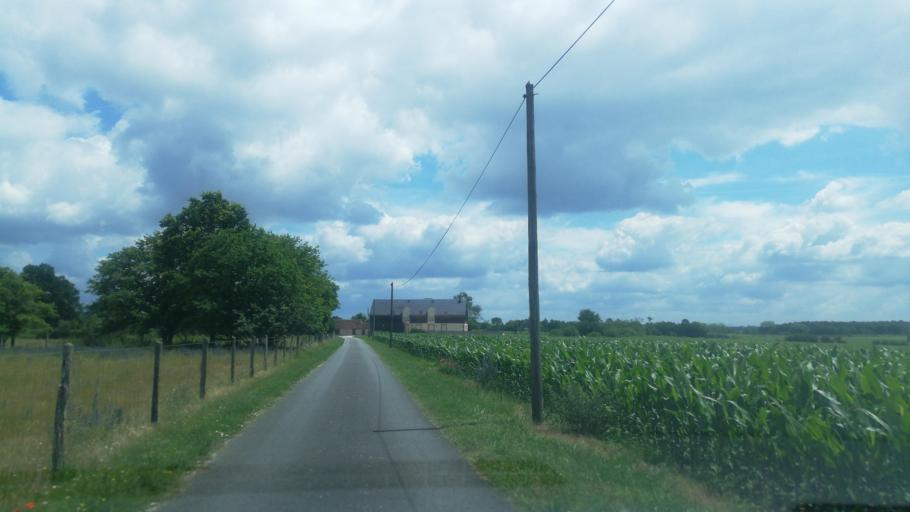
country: FR
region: Centre
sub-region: Departement du Loir-et-Cher
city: Contres
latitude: 47.3633
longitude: 1.4536
